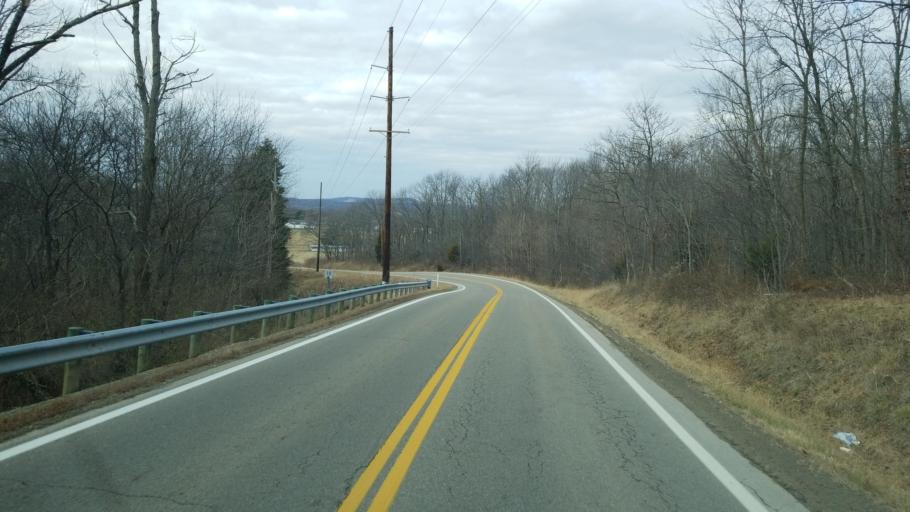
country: US
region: Ohio
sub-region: Ross County
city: Frankfort
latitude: 39.3473
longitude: -83.1932
